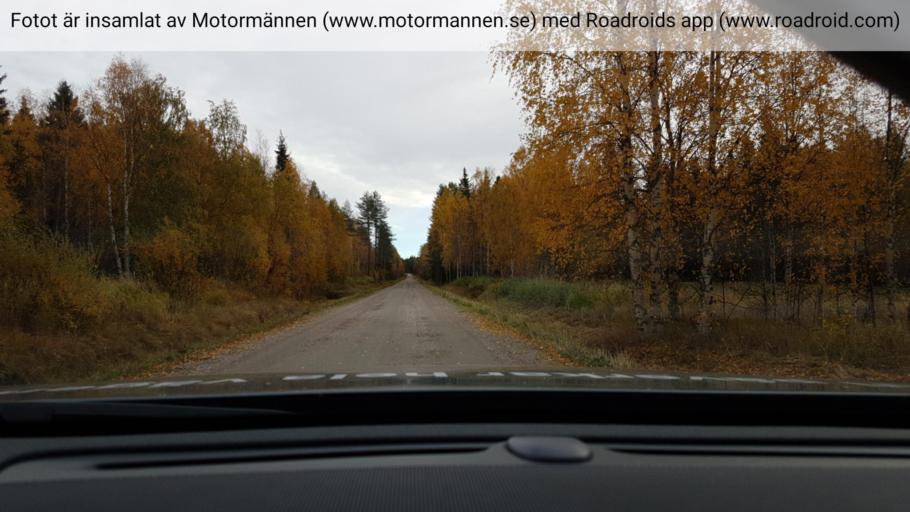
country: SE
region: Norrbotten
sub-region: Overkalix Kommun
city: OEverkalix
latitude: 66.2959
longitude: 22.9432
